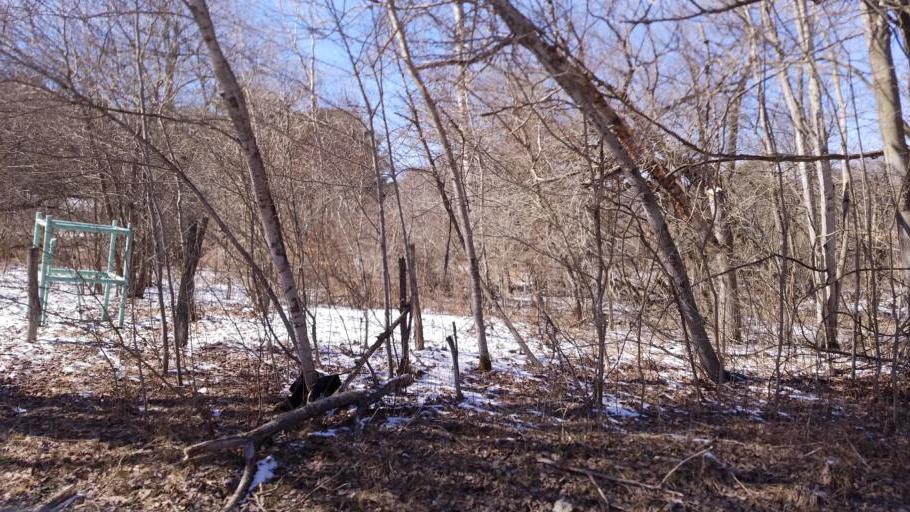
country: US
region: Pennsylvania
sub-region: Tioga County
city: Westfield
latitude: 41.9391
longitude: -77.7319
